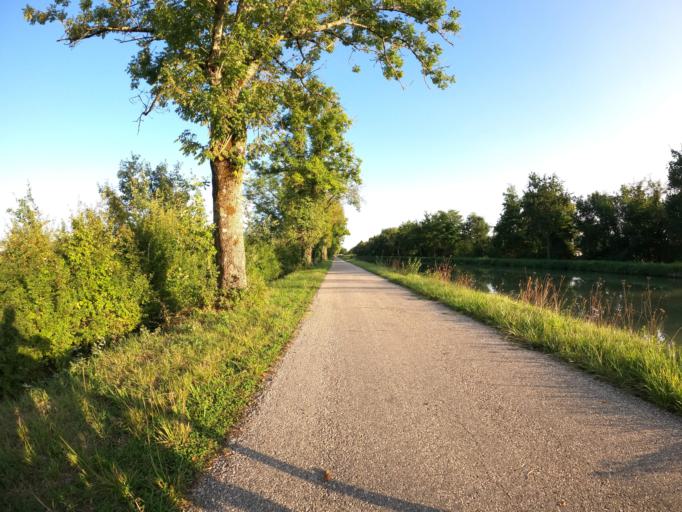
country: FR
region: Midi-Pyrenees
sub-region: Departement du Tarn-et-Garonne
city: Saint-Porquier
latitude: 44.0207
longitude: 1.1665
